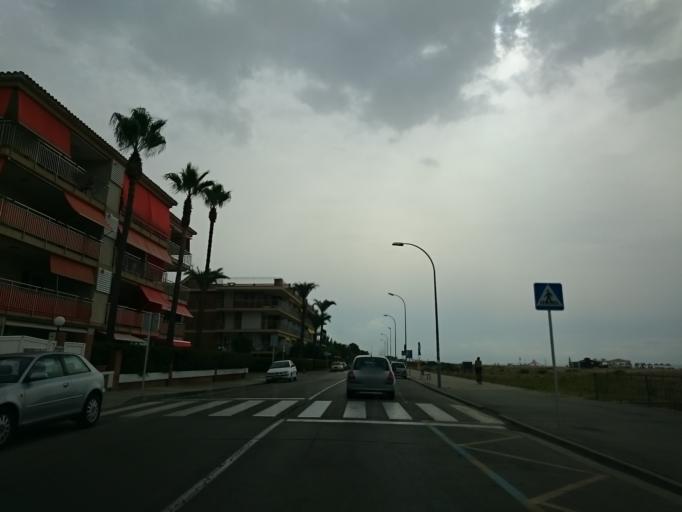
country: ES
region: Catalonia
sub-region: Provincia de Barcelona
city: Castelldefels
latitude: 41.2640
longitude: 1.9394
